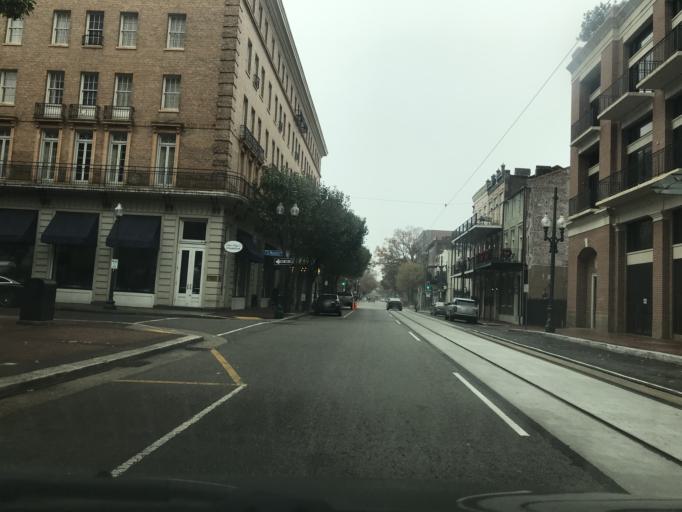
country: US
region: Louisiana
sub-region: Orleans Parish
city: New Orleans
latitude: 29.9481
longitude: -90.0710
